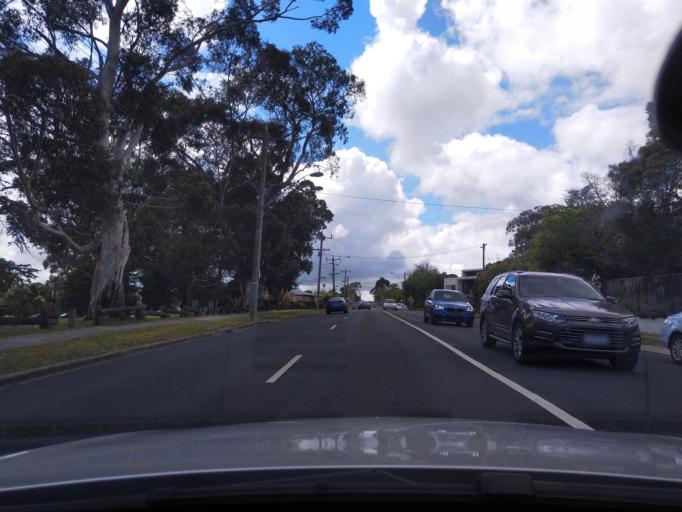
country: AU
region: Victoria
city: Macleod
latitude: -37.7415
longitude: 145.0673
